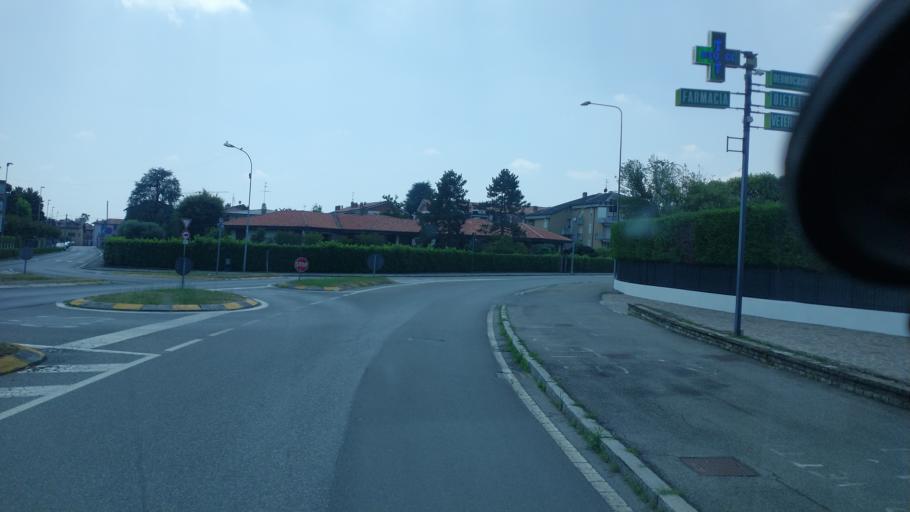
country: IT
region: Lombardy
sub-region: Provincia di Bergamo
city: Calvenzano
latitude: 45.4983
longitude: 9.5992
